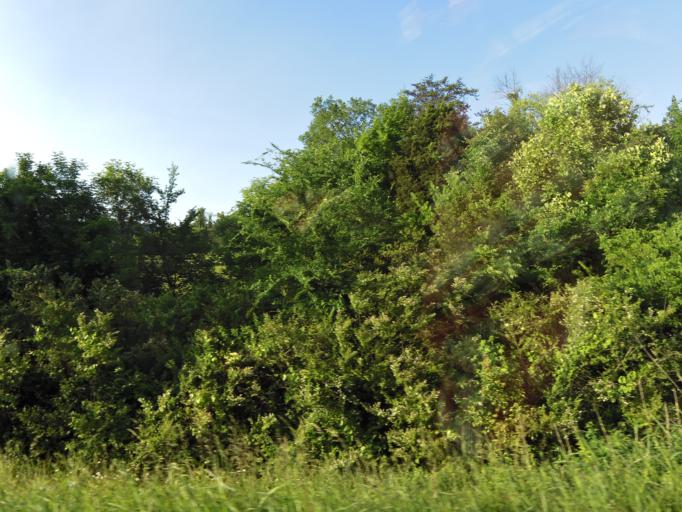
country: US
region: Tennessee
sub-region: Sevier County
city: Seymour
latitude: 35.8803
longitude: -83.7794
